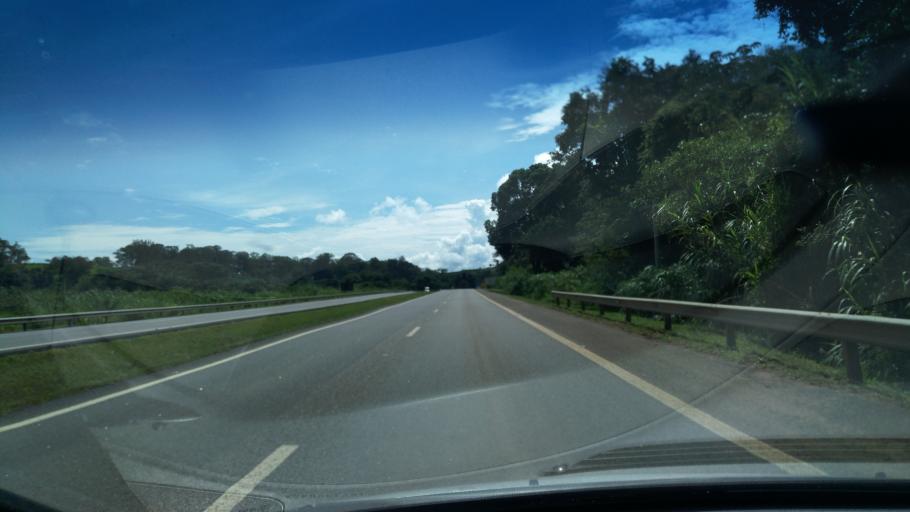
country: BR
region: Sao Paulo
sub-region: Santo Antonio Do Jardim
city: Espirito Santo do Pinhal
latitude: -22.2285
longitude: -46.7948
